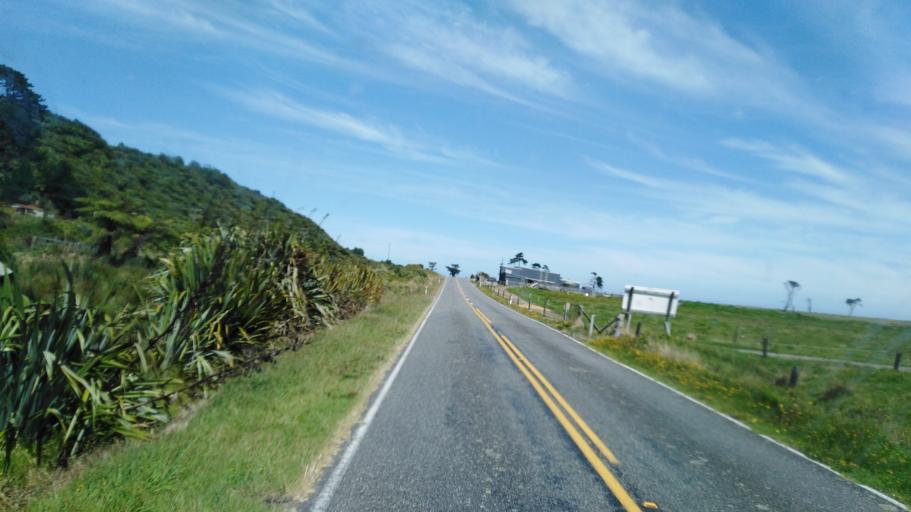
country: NZ
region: West Coast
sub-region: Buller District
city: Westport
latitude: -41.5327
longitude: 171.9381
